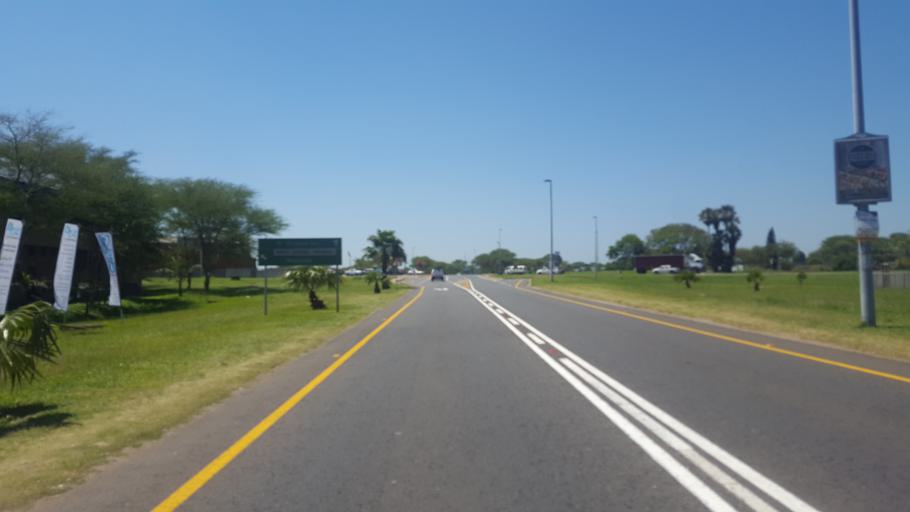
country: ZA
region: KwaZulu-Natal
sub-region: uThungulu District Municipality
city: Richards Bay
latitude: -28.7520
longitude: 32.0548
